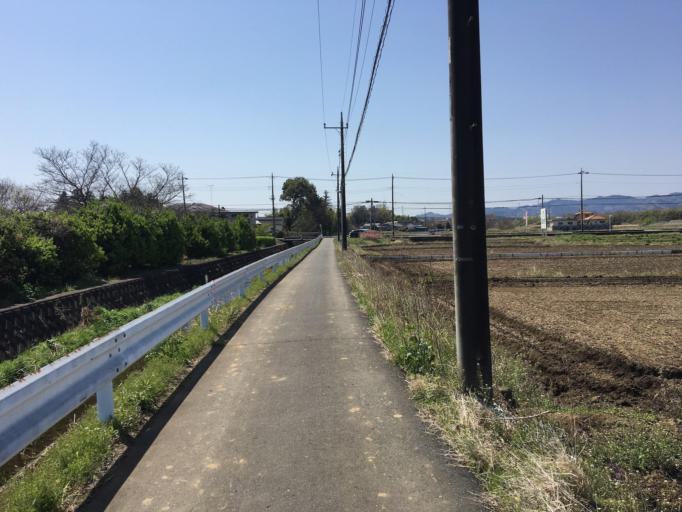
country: JP
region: Saitama
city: Sakado
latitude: 35.9466
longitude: 139.3499
